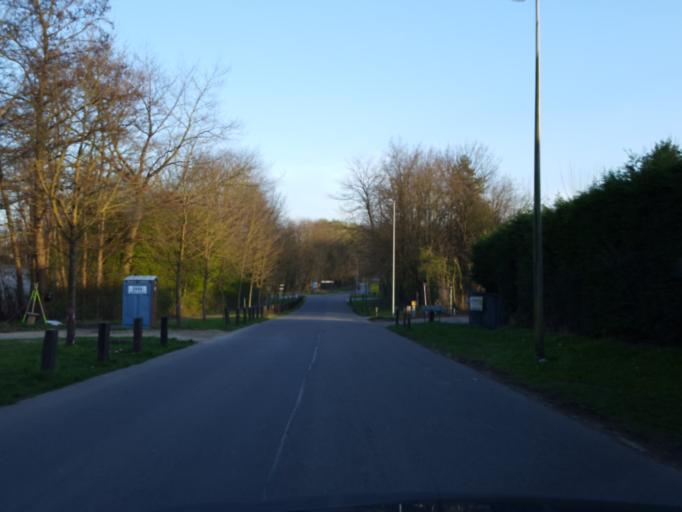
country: BE
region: Wallonia
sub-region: Province du Brabant Wallon
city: Louvain-la-Neuve
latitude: 50.6634
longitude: 4.6344
